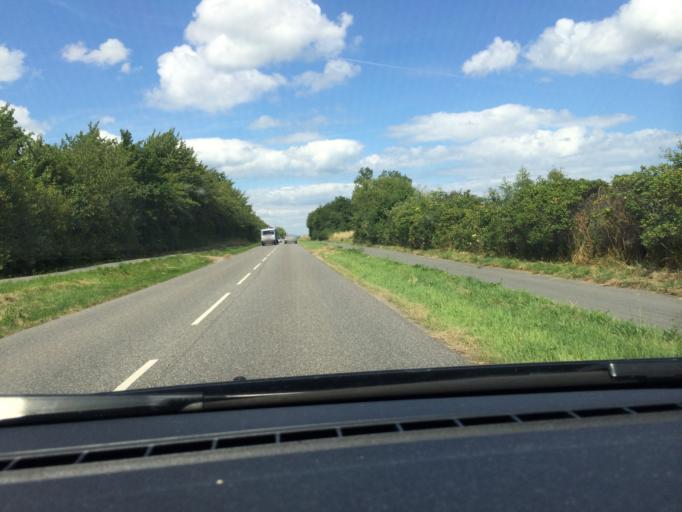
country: DK
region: Zealand
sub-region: Vordingborg Kommune
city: Stege
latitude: 54.9980
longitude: 12.2838
